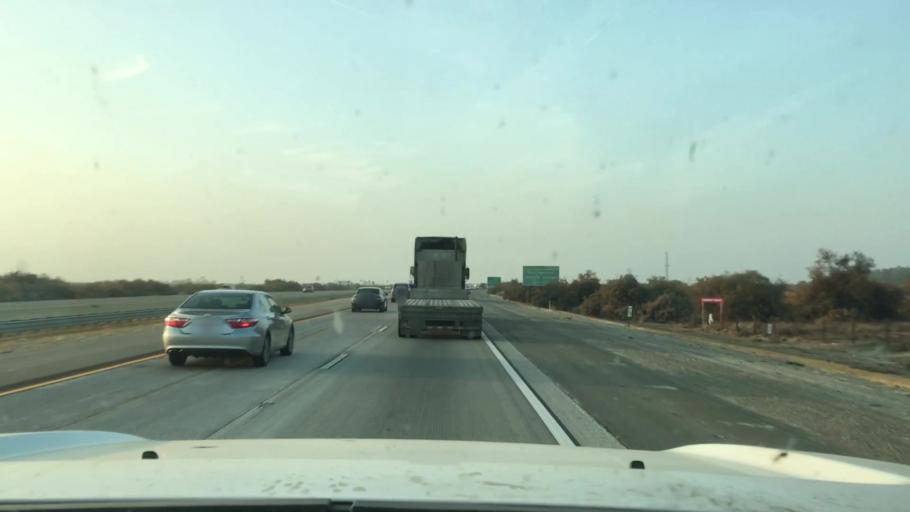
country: US
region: California
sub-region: Kern County
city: Lost Hills
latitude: 35.6039
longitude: -119.6433
